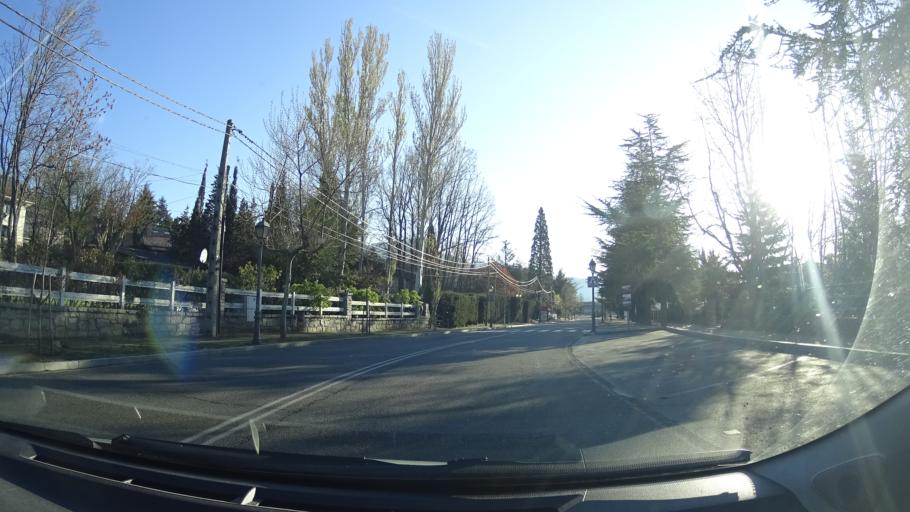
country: ES
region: Madrid
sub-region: Provincia de Madrid
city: Navacerrada
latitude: 40.7237
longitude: -4.0219
